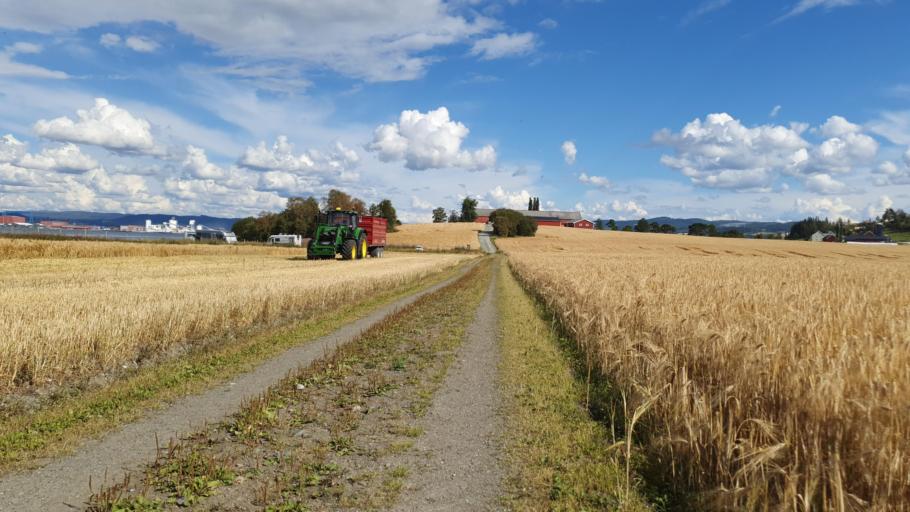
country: NO
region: Nord-Trondelag
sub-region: Verdal
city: Verdal
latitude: 63.7776
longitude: 11.3891
